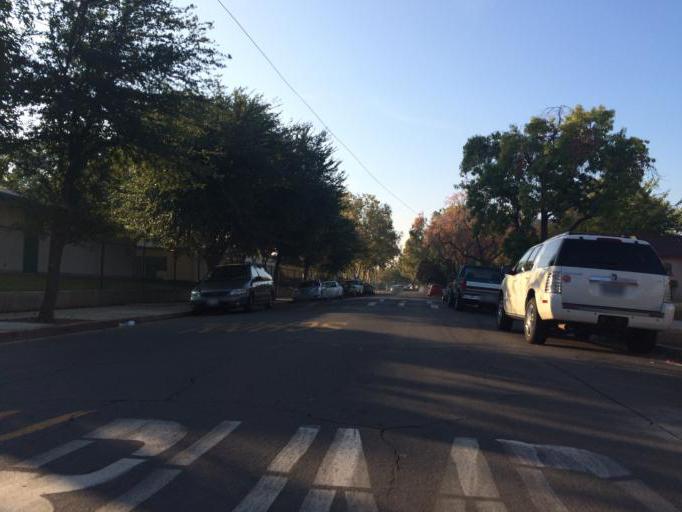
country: US
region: California
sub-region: Fresno County
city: Fresno
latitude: 36.7449
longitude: -119.7793
